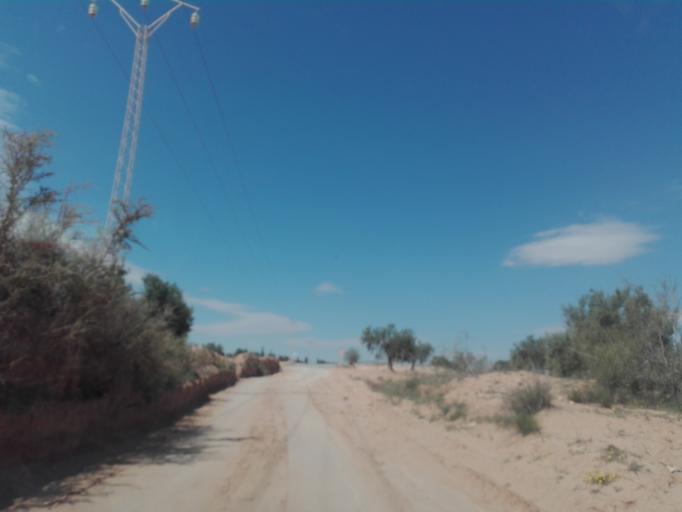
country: TN
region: Safaqis
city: Sfax
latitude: 34.6866
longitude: 10.5572
